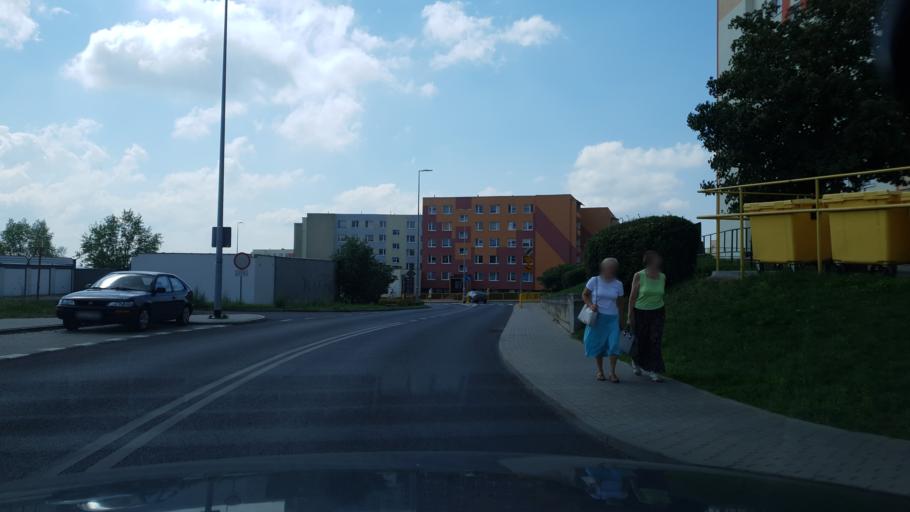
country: PL
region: Kujawsko-Pomorskie
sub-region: Grudziadz
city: Grudziadz
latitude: 53.4559
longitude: 18.7195
